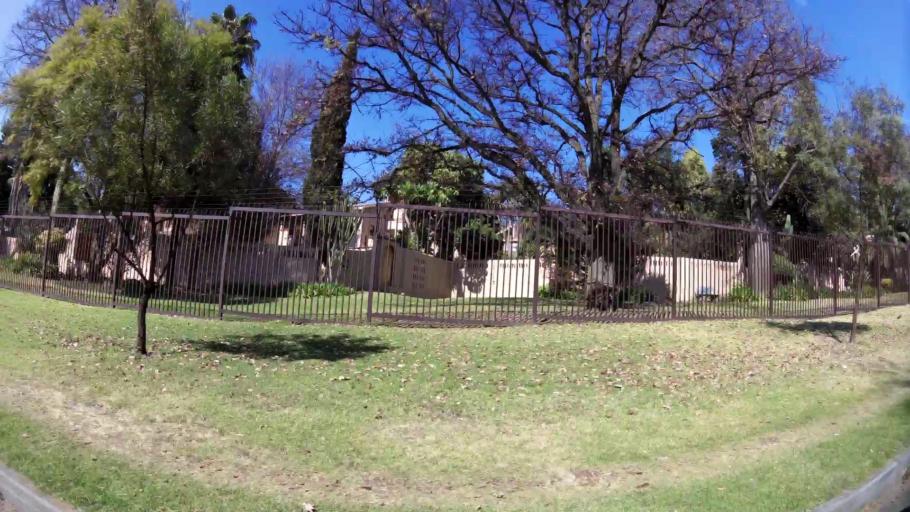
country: ZA
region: Gauteng
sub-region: City of Johannesburg Metropolitan Municipality
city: Johannesburg
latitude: -26.1614
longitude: 28.1150
